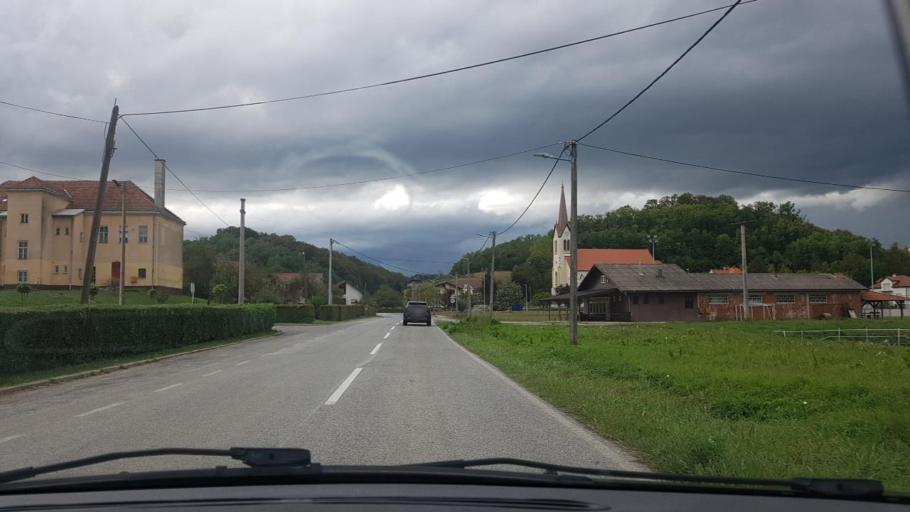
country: HR
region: Zagrebacka
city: Jakovlje
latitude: 45.9587
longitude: 15.8219
